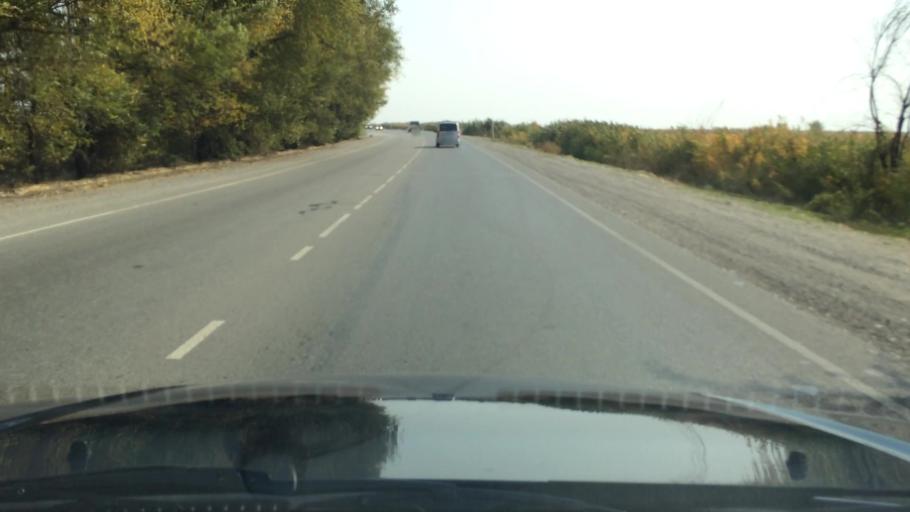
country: KG
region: Chuy
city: Lebedinovka
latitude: 42.9206
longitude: 74.7109
